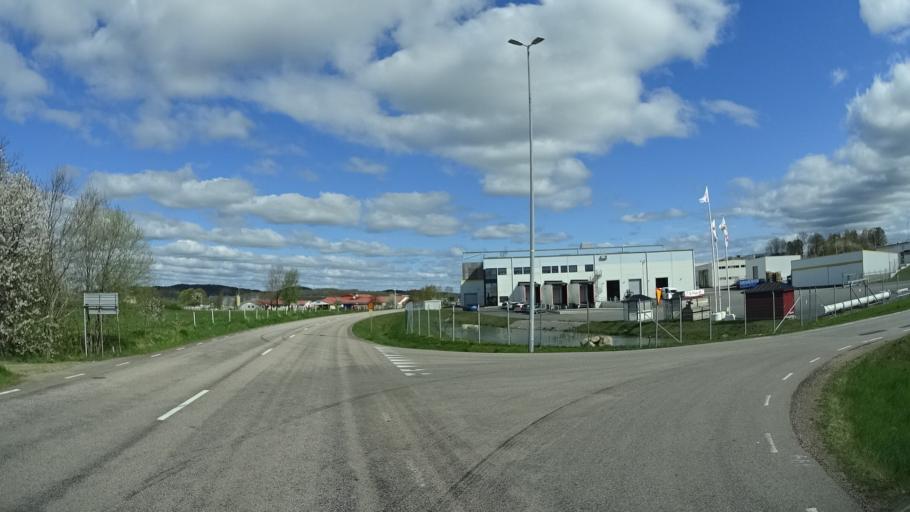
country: SE
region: Halland
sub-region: Halmstads Kommun
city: Getinge
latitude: 56.8546
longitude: 12.6808
